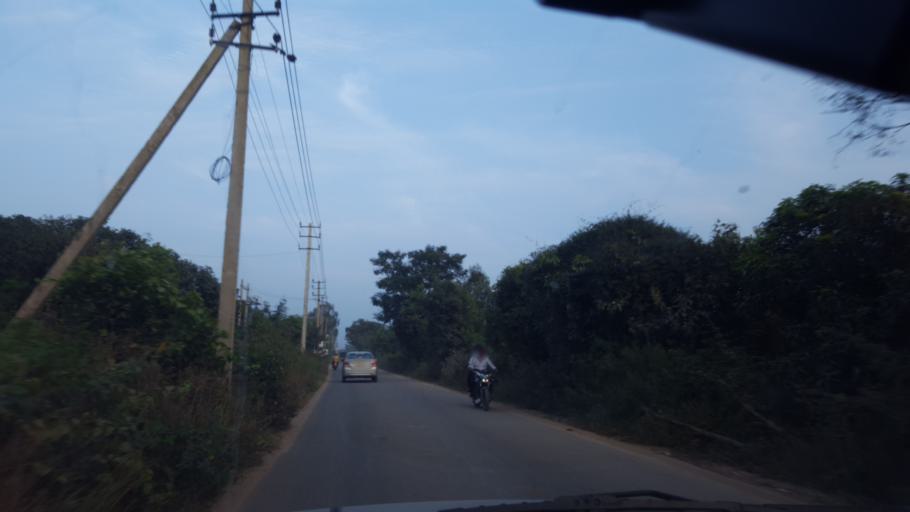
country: IN
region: Karnataka
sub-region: Bangalore Rural
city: Hoskote
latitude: 13.0770
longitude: 77.6989
